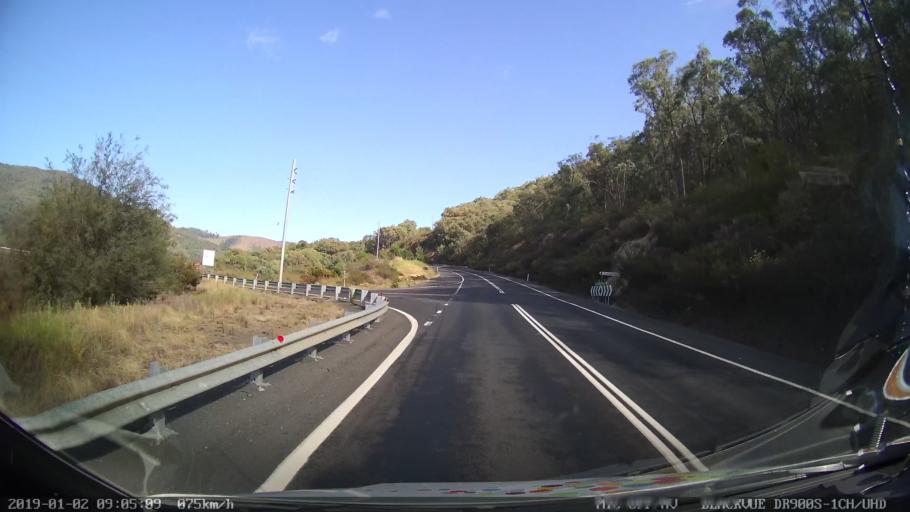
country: AU
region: New South Wales
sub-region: Tumut Shire
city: Tumut
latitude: -35.5625
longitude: 148.3122
